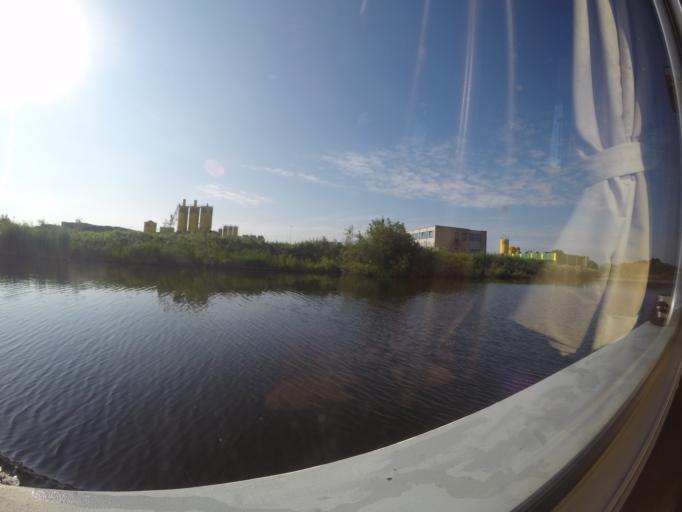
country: NL
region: Overijssel
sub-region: Gemeente Wierden
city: Wierden
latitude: 52.3673
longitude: 6.6255
